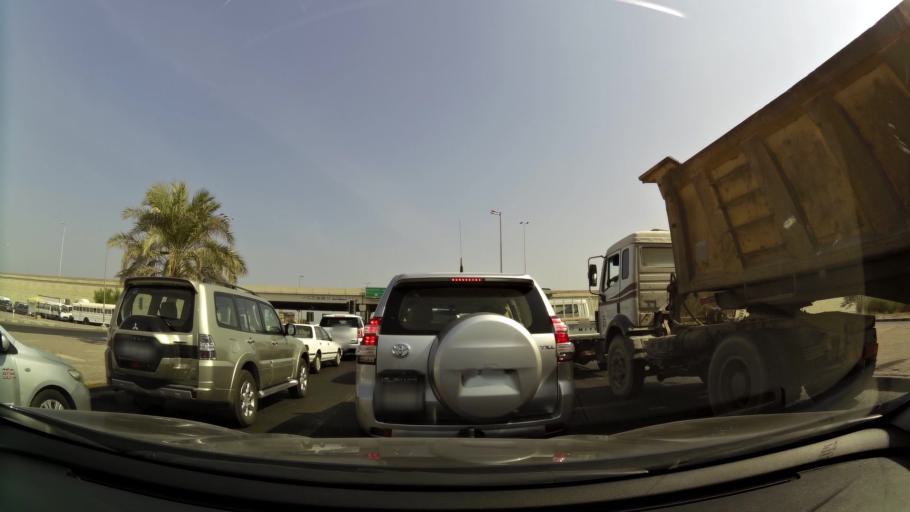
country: KW
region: Al Ahmadi
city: Al Fahahil
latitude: 29.0908
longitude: 48.1149
